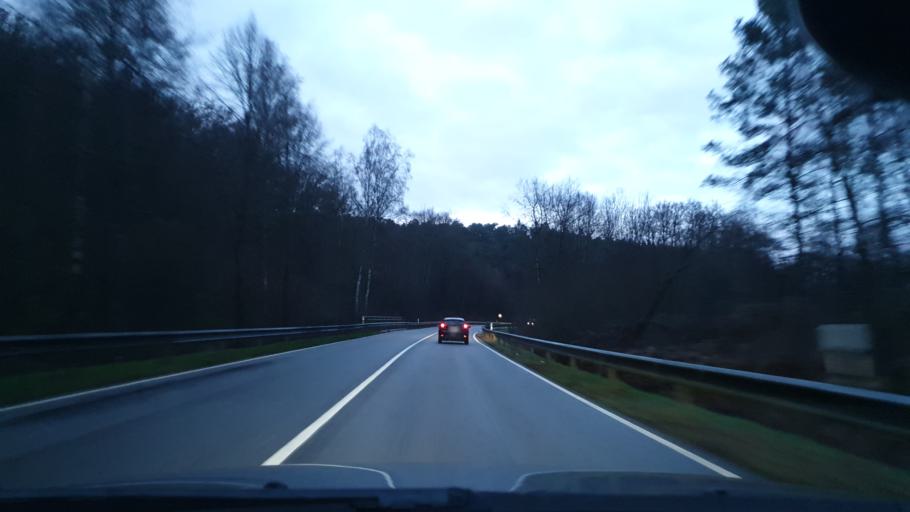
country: DE
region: Rheinland-Pfalz
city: Schopp
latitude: 49.3660
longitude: 7.6929
